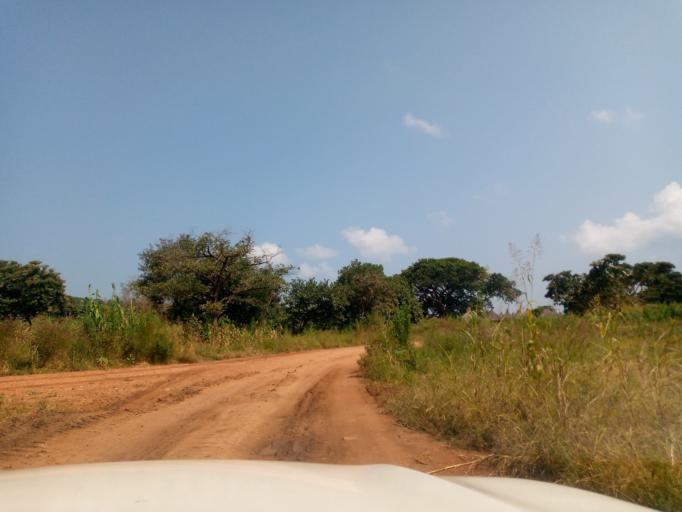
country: ET
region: Oromiya
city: Mendi
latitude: 10.2072
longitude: 35.0764
